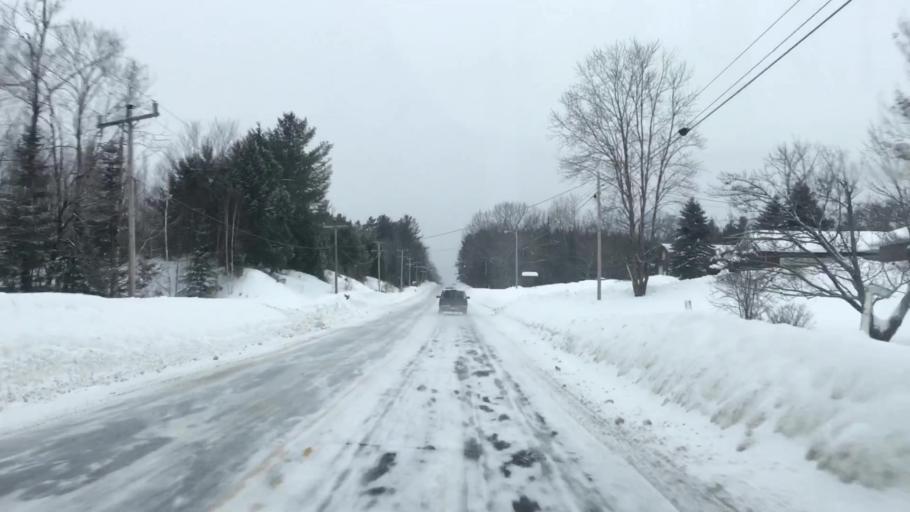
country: US
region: Maine
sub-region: Penobscot County
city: Medway
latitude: 45.5994
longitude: -68.4697
